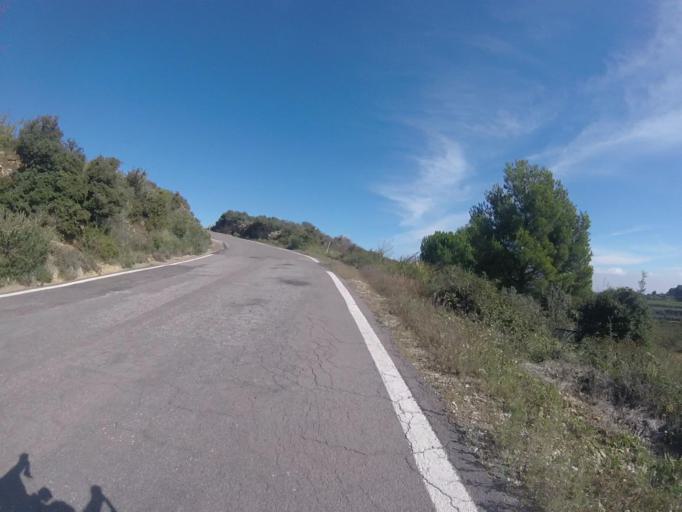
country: ES
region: Valencia
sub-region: Provincia de Castello
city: Sarratella
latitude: 40.3161
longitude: 0.0301
